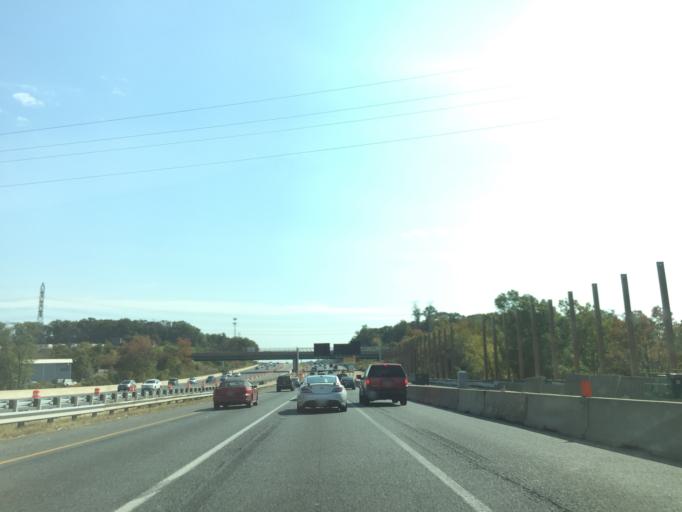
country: US
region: Maryland
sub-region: Baltimore County
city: Overlea
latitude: 39.3634
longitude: -76.5075
